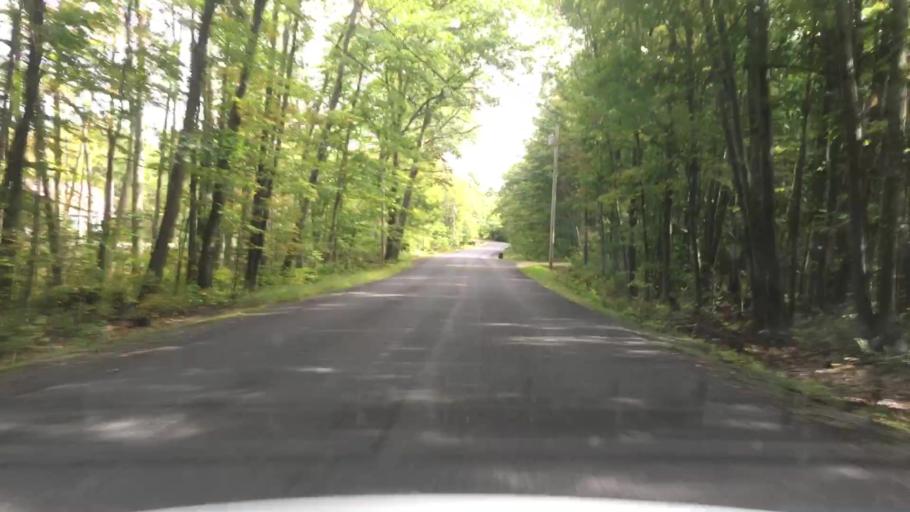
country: US
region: Maine
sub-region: Androscoggin County
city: Lisbon Falls
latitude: 43.9601
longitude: -70.0542
